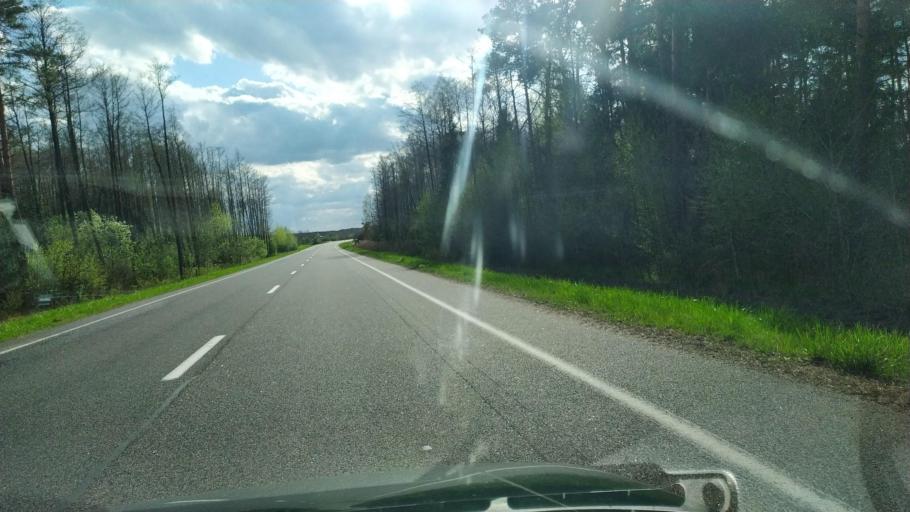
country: BY
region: Brest
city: Pruzhany
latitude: 52.6992
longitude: 24.2766
